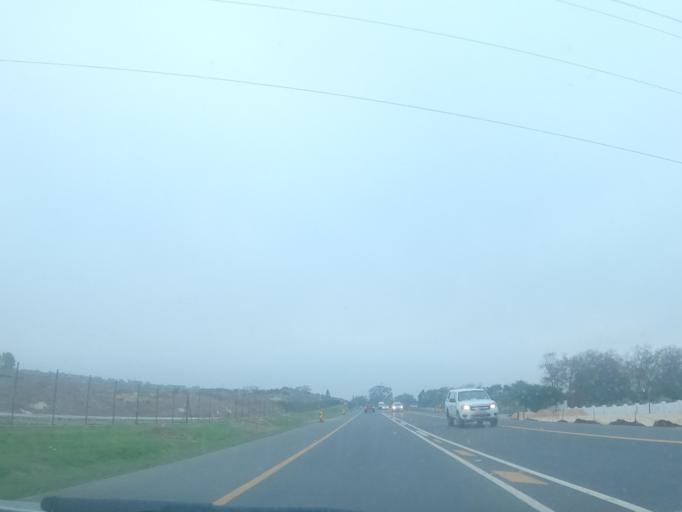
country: ZA
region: Western Cape
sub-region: Cape Winelands District Municipality
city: Stellenbosch
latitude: -33.9531
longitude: 18.7908
